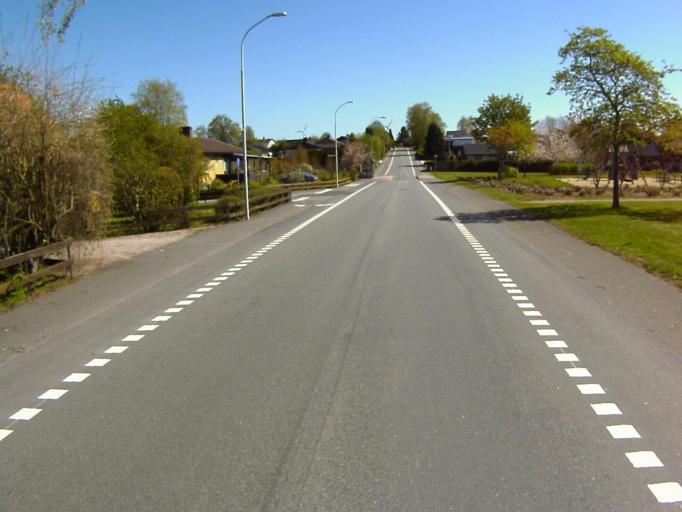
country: SE
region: Skane
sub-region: Kristianstads Kommun
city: Kristianstad
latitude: 56.0494
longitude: 14.2065
